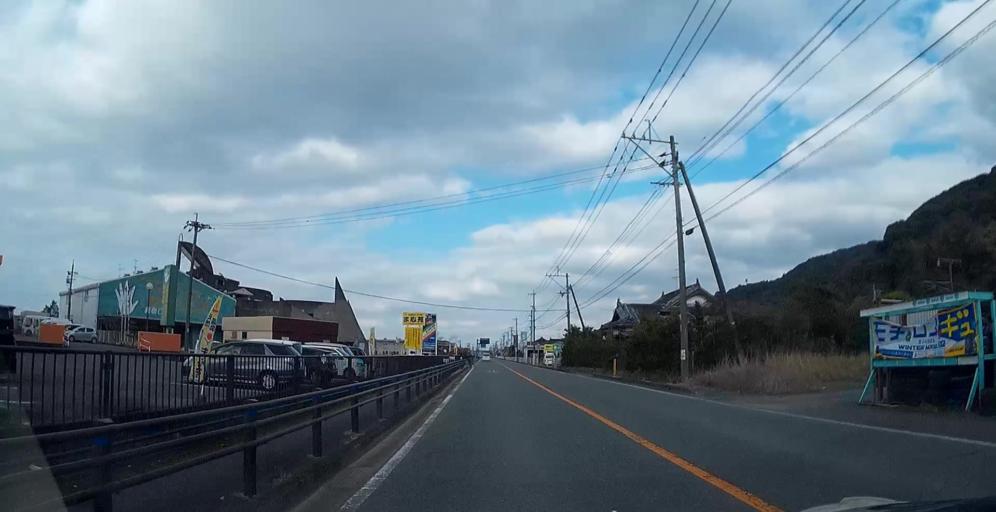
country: JP
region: Kumamoto
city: Yatsushiro
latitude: 32.4572
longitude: 130.5997
